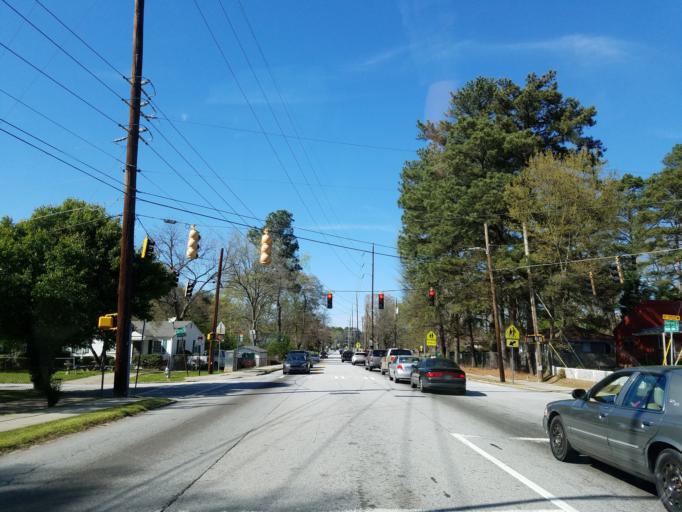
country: US
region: Georgia
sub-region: Fulton County
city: Atlanta
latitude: 33.7592
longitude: -84.4693
